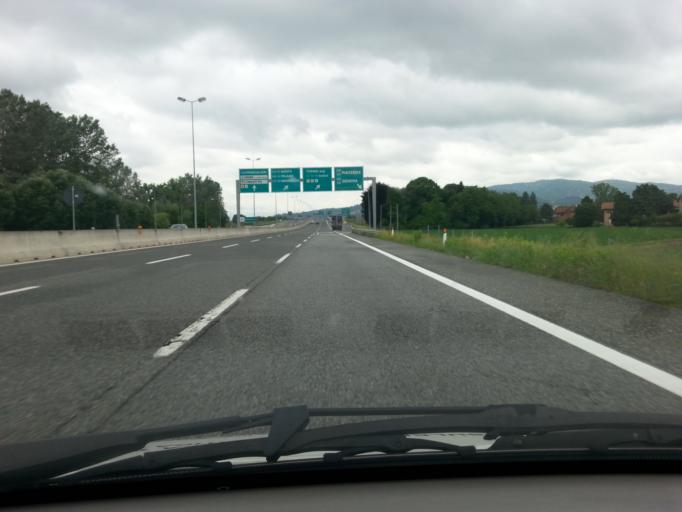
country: IT
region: Piedmont
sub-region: Provincia di Torino
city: La Loggia
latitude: 44.9653
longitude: 7.7041
